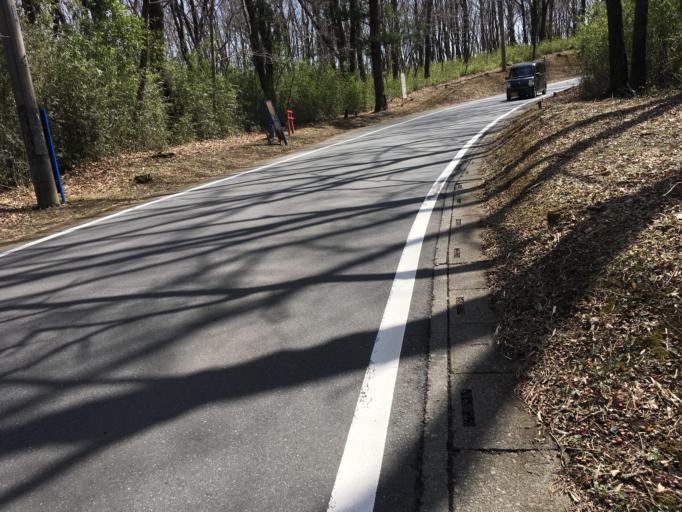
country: JP
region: Saitama
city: Ogawa
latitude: 36.0160
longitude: 139.3290
